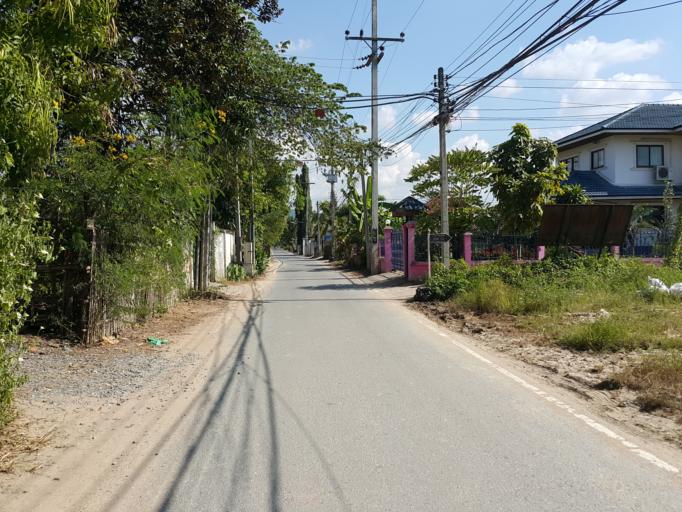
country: TH
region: Chiang Mai
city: San Kamphaeng
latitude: 18.7802
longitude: 99.1603
